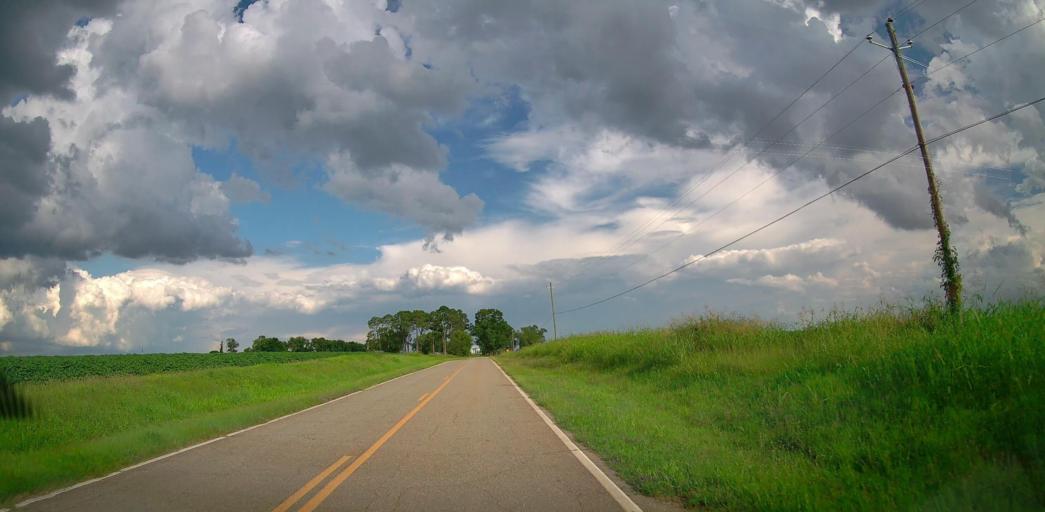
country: US
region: Georgia
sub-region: Bleckley County
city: Cochran
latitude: 32.4025
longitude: -83.3775
